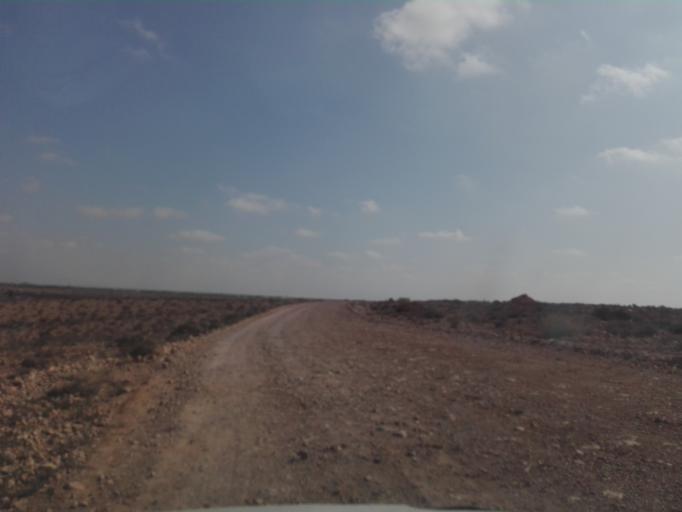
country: TN
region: Madanin
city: Medenine
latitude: 33.4315
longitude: 10.4103
